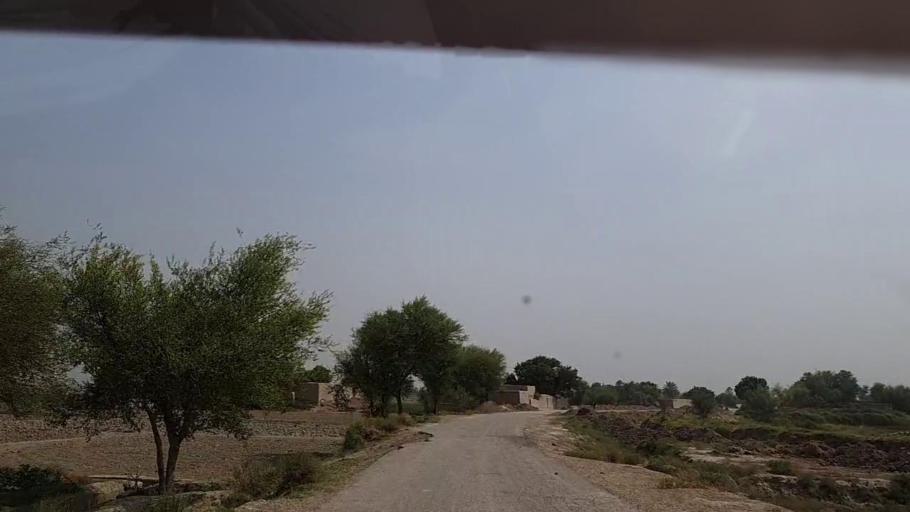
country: PK
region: Sindh
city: Khairpur Nathan Shah
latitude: 27.0551
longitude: 67.6843
